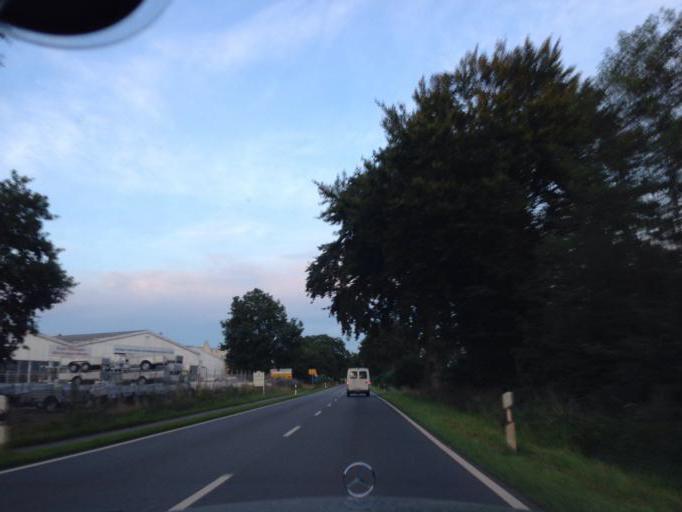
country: DE
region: Schleswig-Holstein
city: Bargteheide
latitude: 53.7196
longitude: 10.2764
